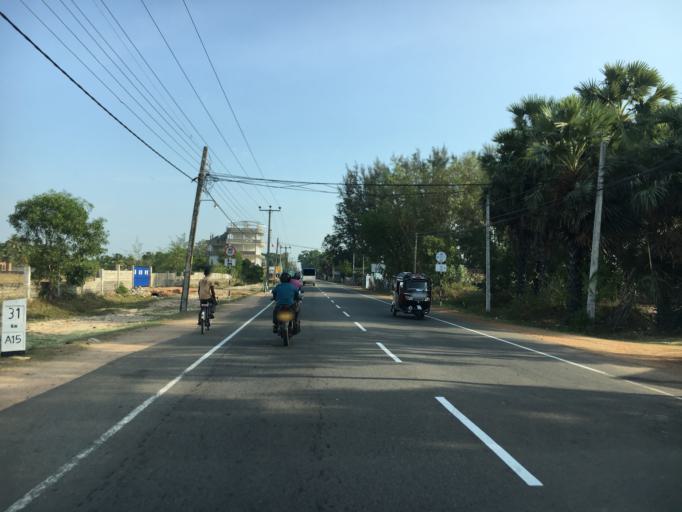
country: LK
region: Eastern Province
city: Eravur Town
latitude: 7.9039
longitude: 81.5348
